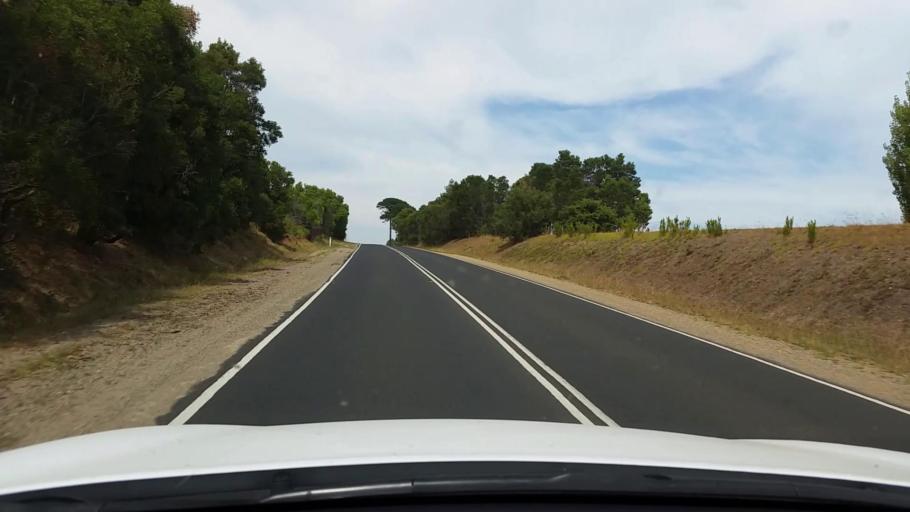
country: AU
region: Victoria
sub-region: Mornington Peninsula
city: Merricks
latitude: -38.4402
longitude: 145.0362
